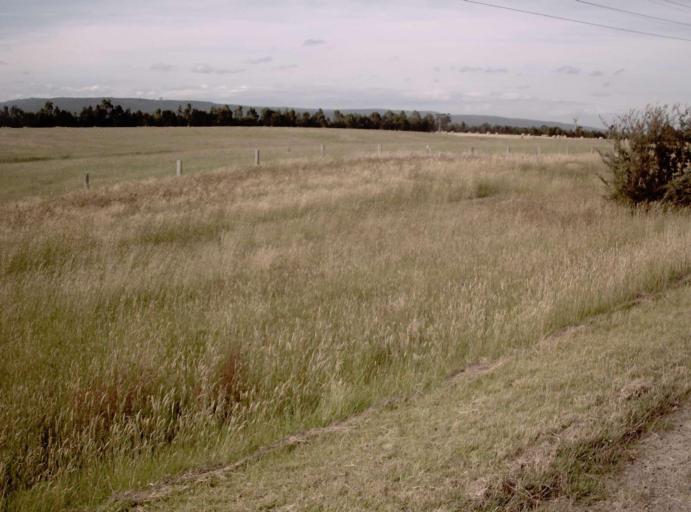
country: AU
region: Victoria
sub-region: Latrobe
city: Traralgon
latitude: -38.1131
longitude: 146.5830
